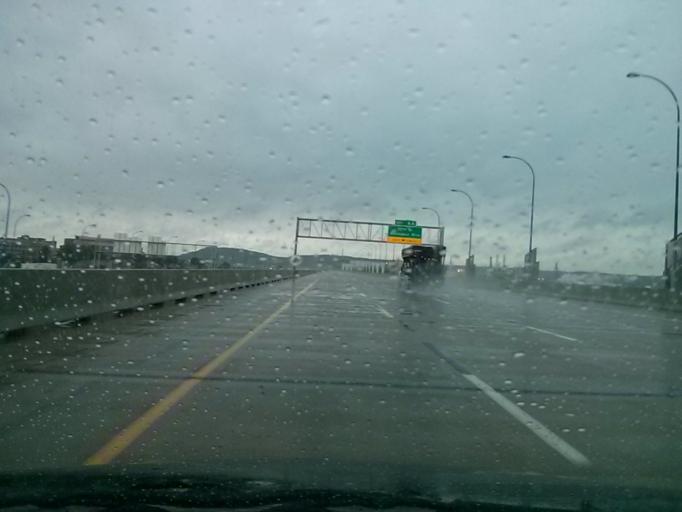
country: US
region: Oklahoma
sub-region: Tulsa County
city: Tulsa
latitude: 36.1449
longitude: -96.0044
